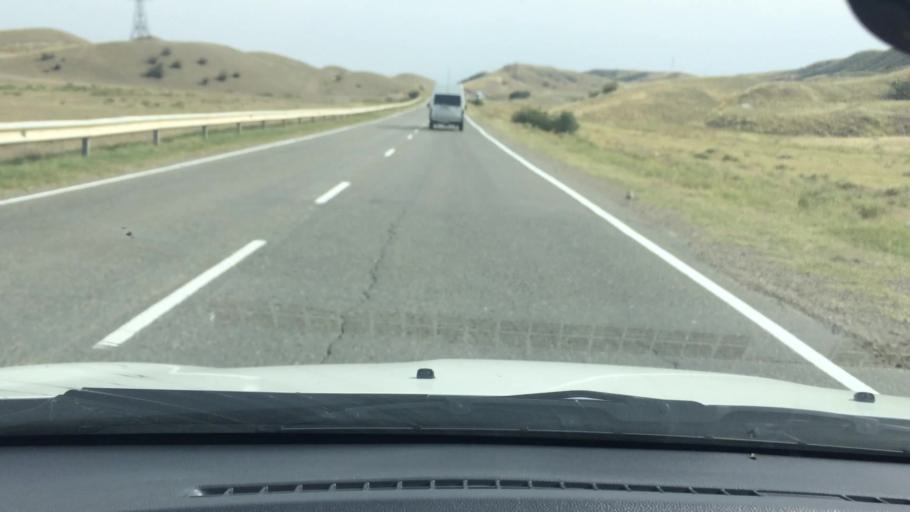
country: GE
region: Kvemo Kartli
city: Rust'avi
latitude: 41.5340
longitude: 44.9811
